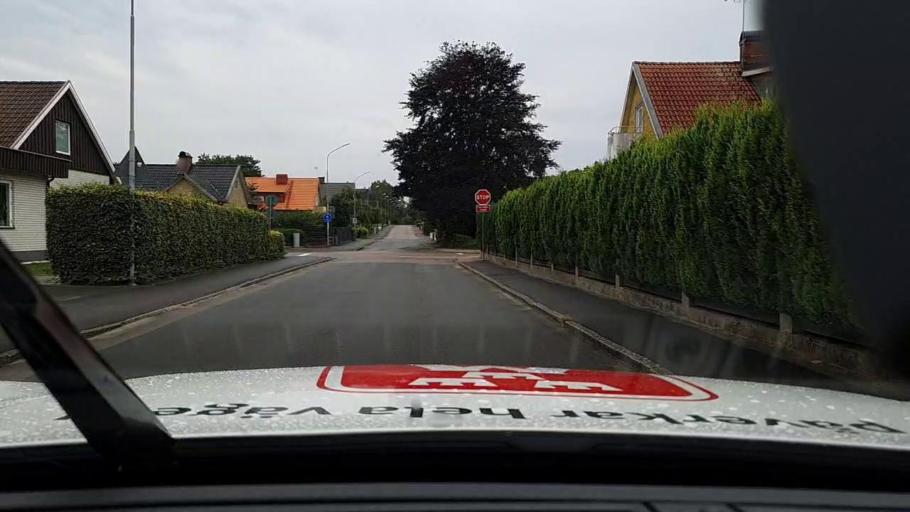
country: SE
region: Skane
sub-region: Hassleholms Kommun
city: Hassleholm
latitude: 56.1649
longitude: 13.7741
